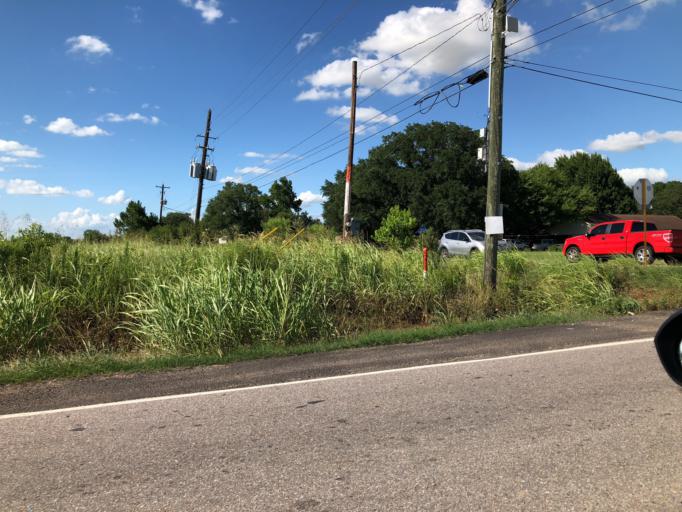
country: US
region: Texas
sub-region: Harris County
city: Katy
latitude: 29.8314
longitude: -95.8071
